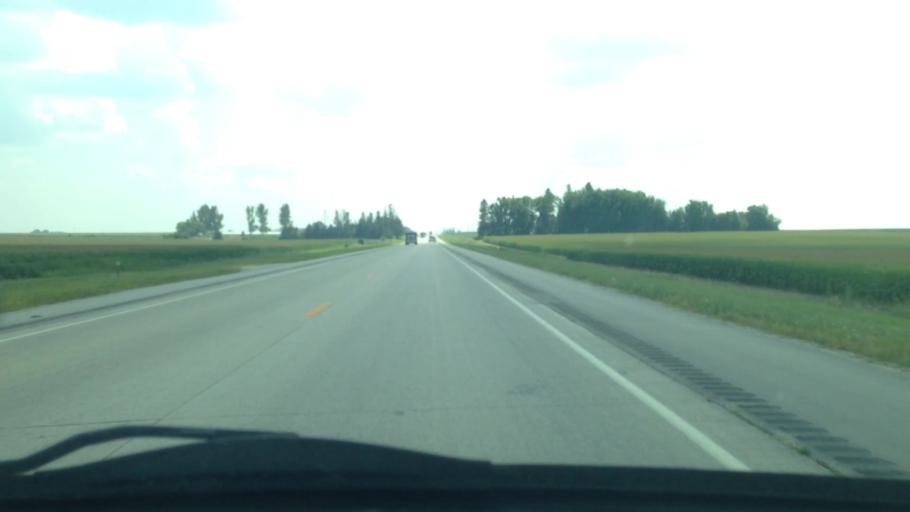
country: US
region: Minnesota
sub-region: Fillmore County
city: Spring Valley
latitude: 43.6680
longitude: -92.3896
